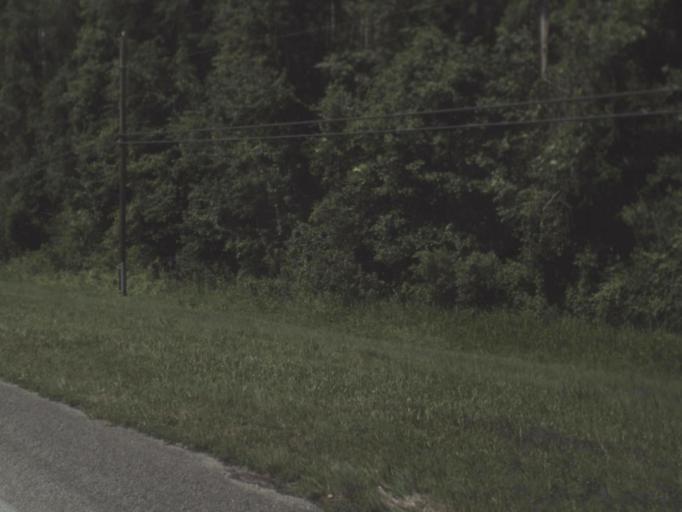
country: US
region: Florida
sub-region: Alachua County
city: Hawthorne
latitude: 29.6470
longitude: -82.1089
